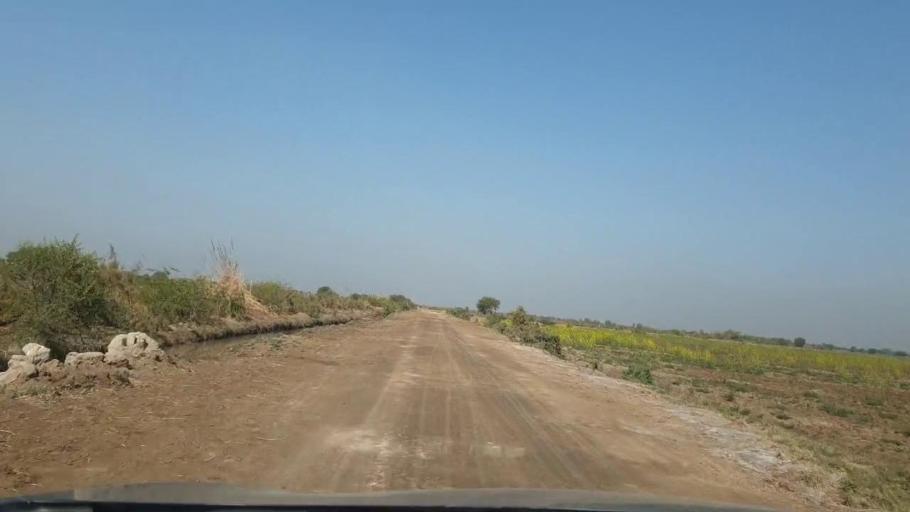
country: PK
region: Sindh
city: Berani
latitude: 25.7099
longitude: 68.8615
